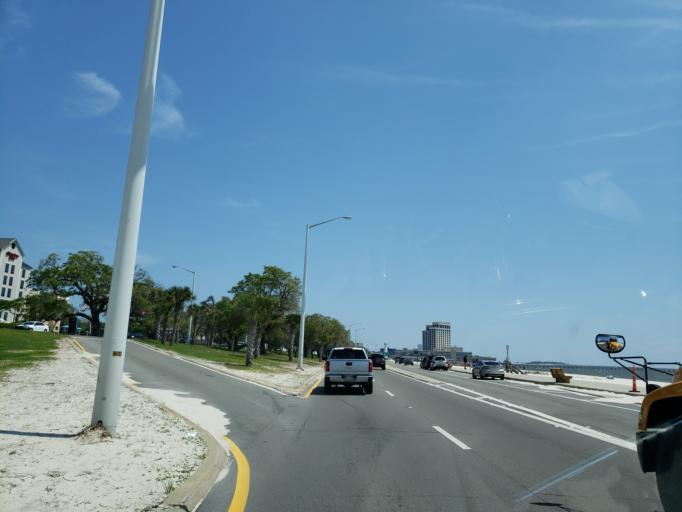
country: US
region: Mississippi
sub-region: Harrison County
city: Biloxi
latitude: 30.3947
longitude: -88.9068
